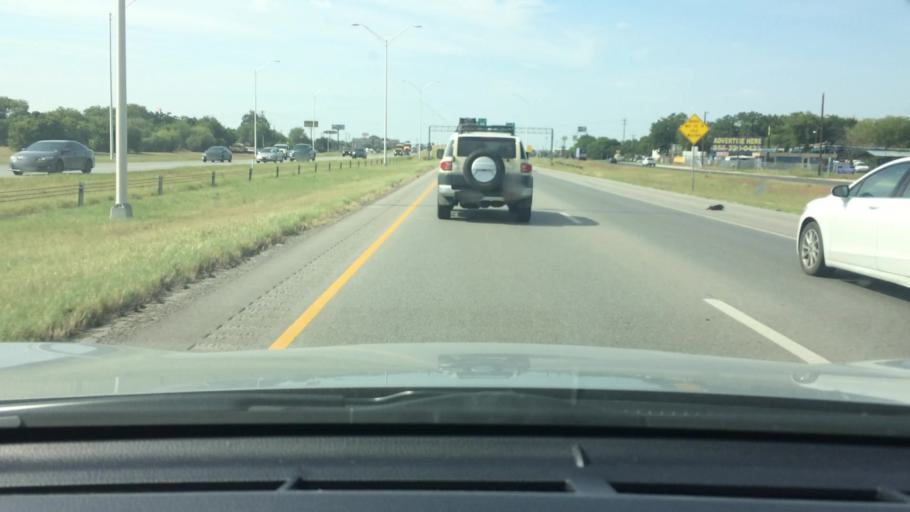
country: US
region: Texas
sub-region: Bexar County
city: China Grove
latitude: 29.3930
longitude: -98.3892
